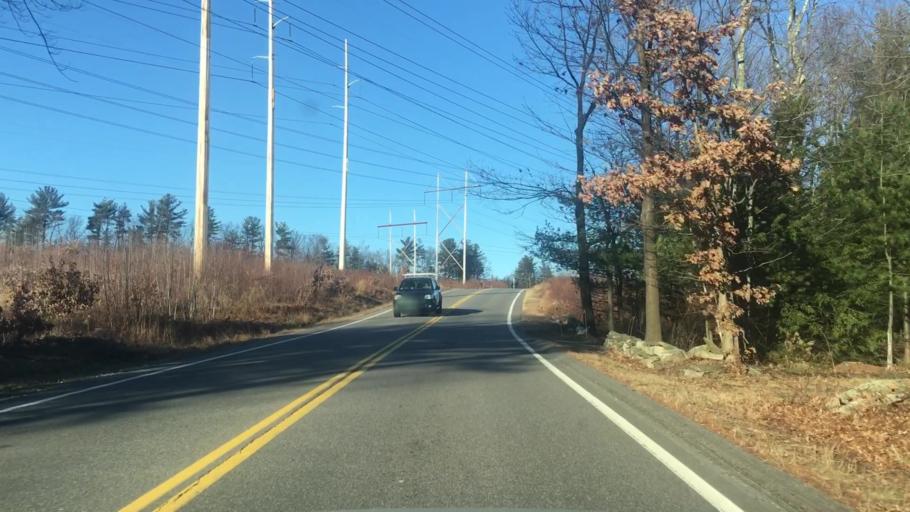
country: US
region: New Hampshire
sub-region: Rockingham County
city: Londonderry
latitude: 42.8877
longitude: -71.3702
